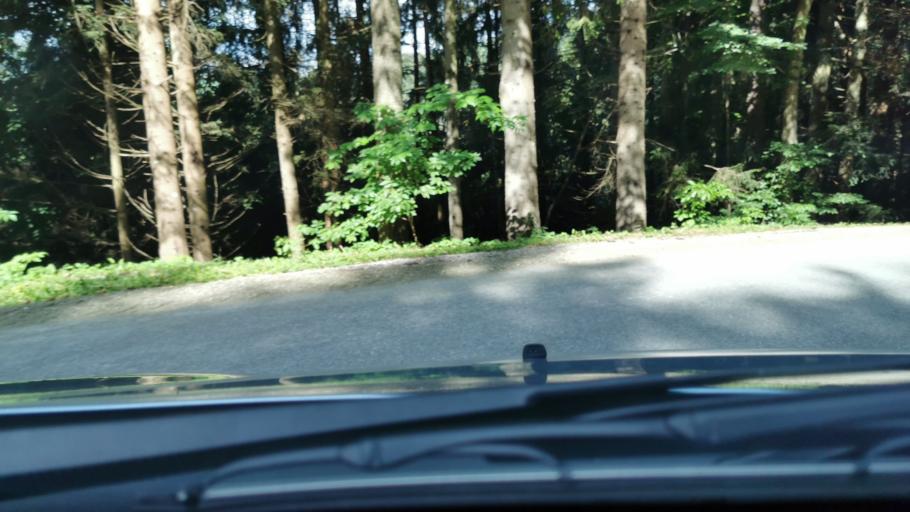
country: AT
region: Styria
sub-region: Politischer Bezirk Weiz
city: Koglhof
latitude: 47.3316
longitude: 15.7001
